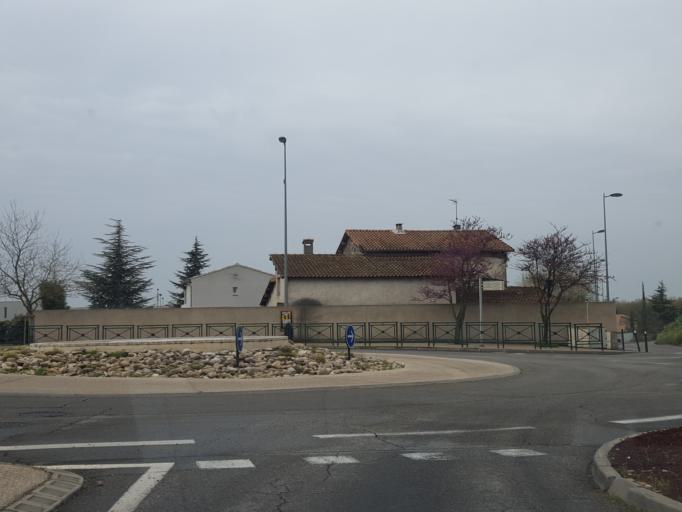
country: FR
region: Provence-Alpes-Cote d'Azur
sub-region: Departement du Vaucluse
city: Morieres-les-Avignon
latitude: 43.9391
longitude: 4.9080
